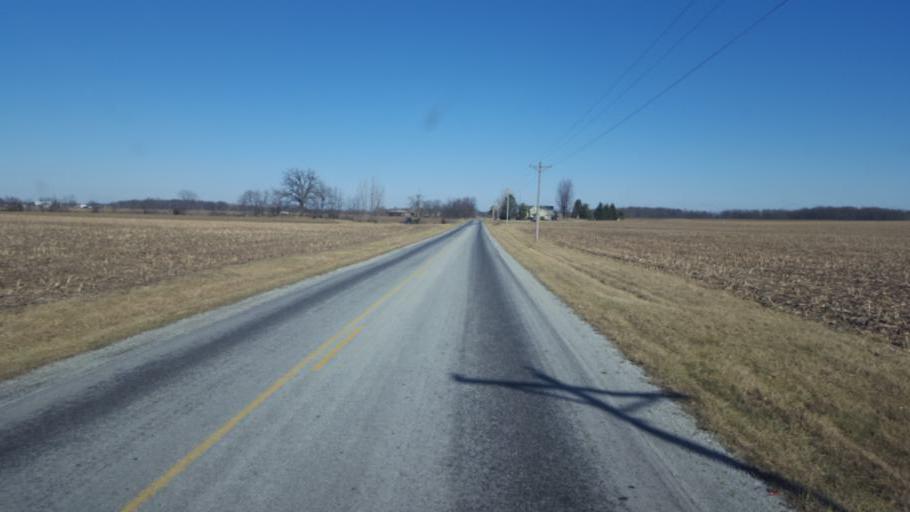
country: US
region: Ohio
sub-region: Hardin County
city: Kenton
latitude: 40.6342
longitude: -83.4835
